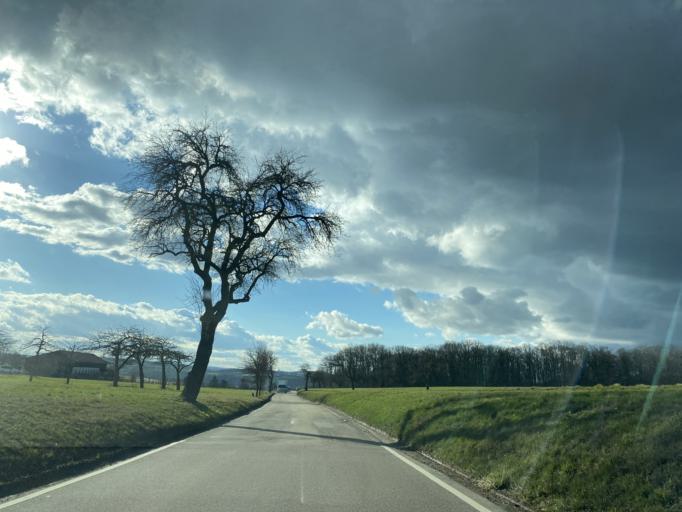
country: DE
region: Baden-Wuerttemberg
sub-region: Regierungsbezirk Stuttgart
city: Eberdingen
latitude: 48.8906
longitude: 8.9910
